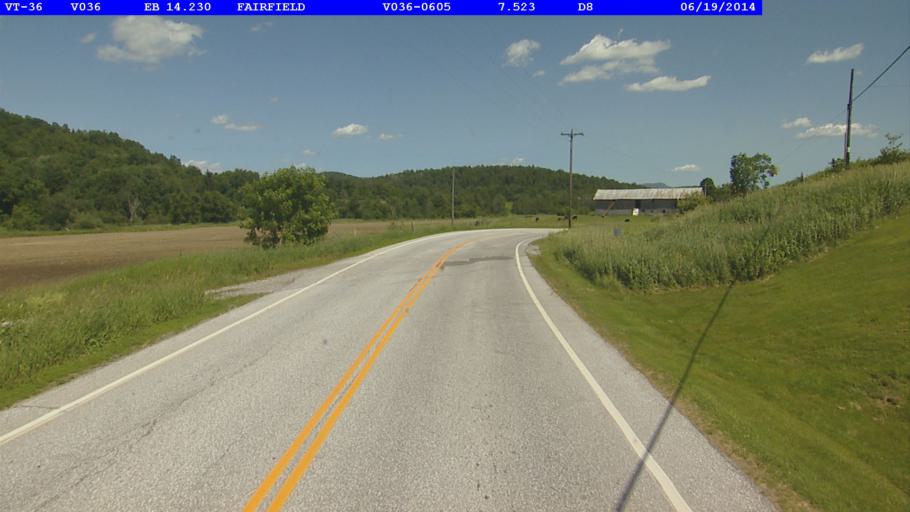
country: US
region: Vermont
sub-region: Franklin County
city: Enosburg Falls
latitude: 44.7992
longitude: -72.8901
